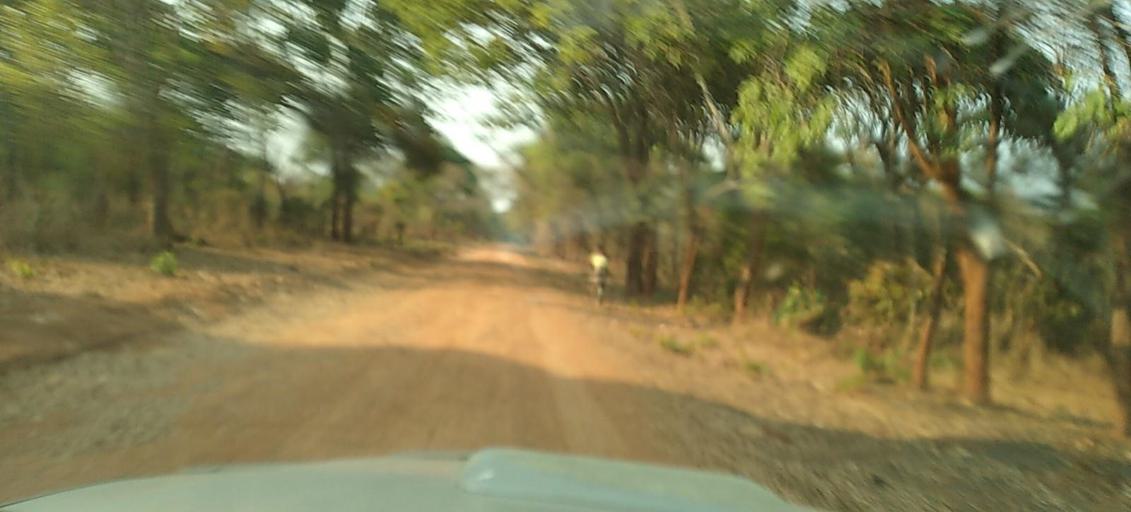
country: ZM
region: North-Western
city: Kasempa
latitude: -13.3130
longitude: 26.5521
